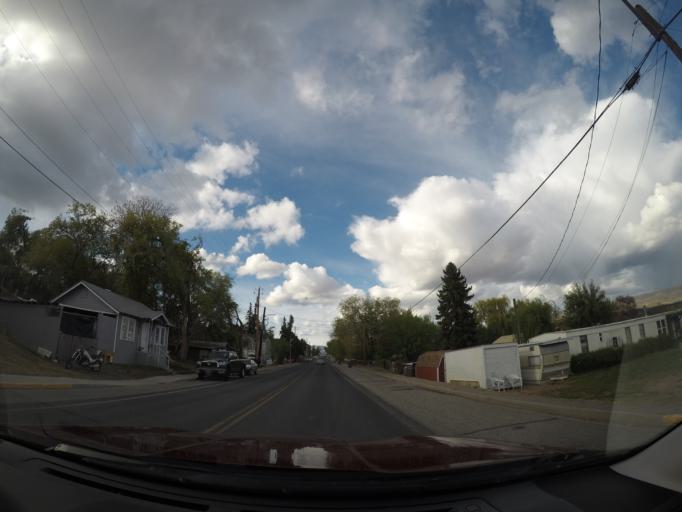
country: US
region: Washington
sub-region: Chelan County
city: South Wenatchee
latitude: 47.3978
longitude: -120.3030
